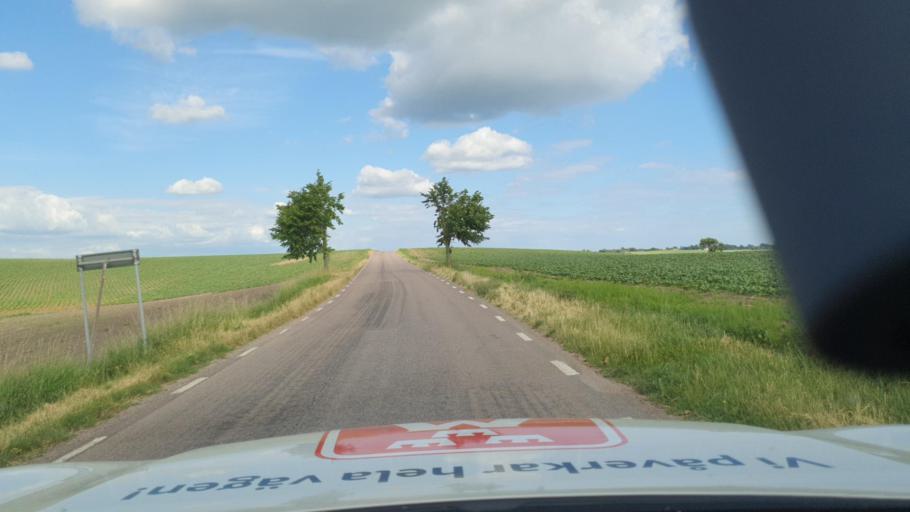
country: SE
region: Skane
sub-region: Skurups Kommun
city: Rydsgard
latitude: 55.4509
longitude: 13.5770
